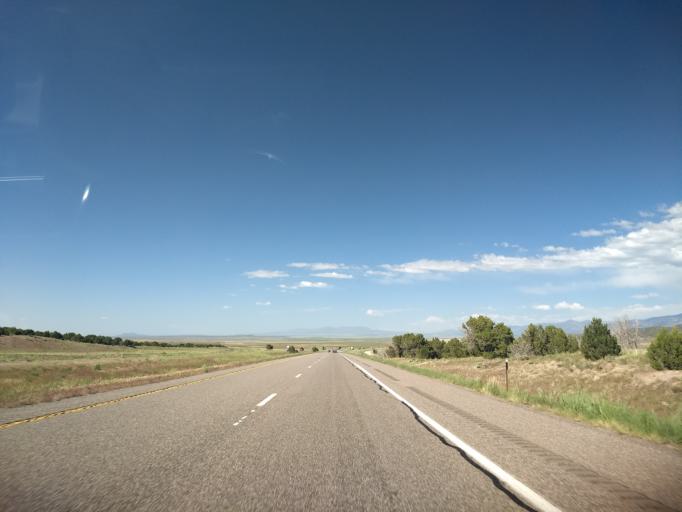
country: US
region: Utah
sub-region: Millard County
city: Fillmore
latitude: 38.7270
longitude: -112.5933
